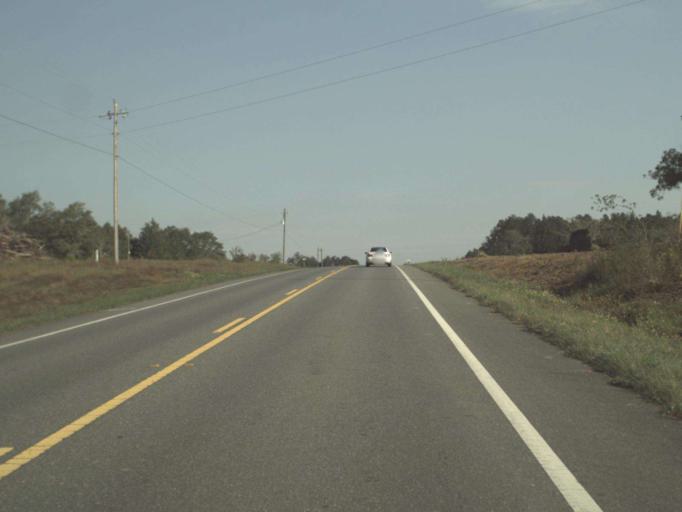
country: US
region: Florida
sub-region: Holmes County
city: Bonifay
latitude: 30.7052
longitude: -85.6860
